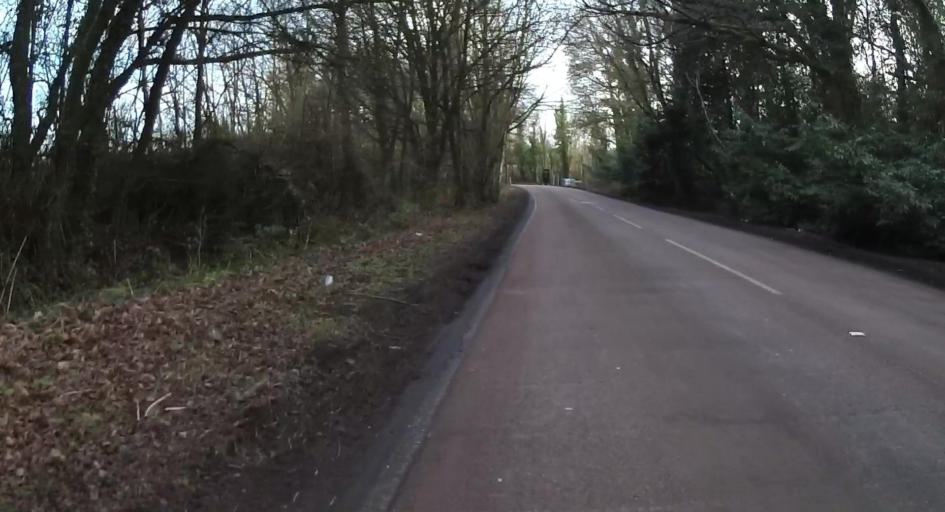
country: GB
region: England
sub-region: Wokingham
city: Wokingham
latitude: 51.3974
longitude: -0.8091
